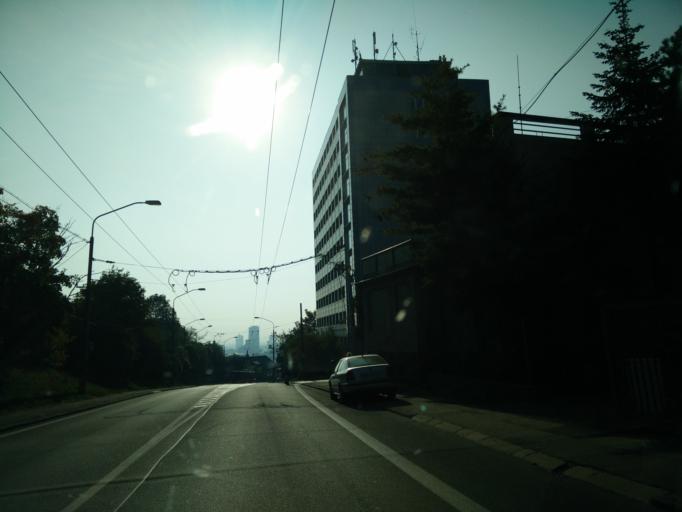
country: SK
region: Bratislavsky
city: Bratislava
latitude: 48.1644
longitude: 17.0970
